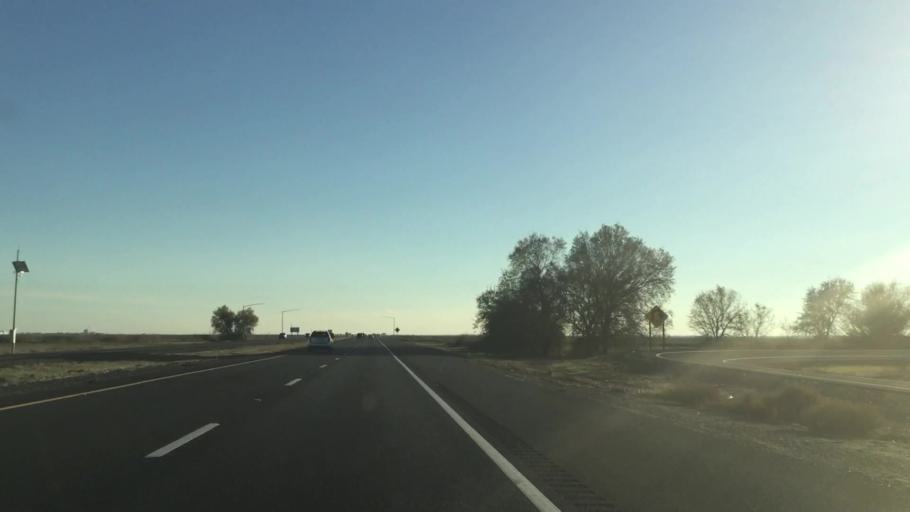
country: US
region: California
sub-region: Sacramento County
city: Elverta
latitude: 38.8167
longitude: -121.5441
